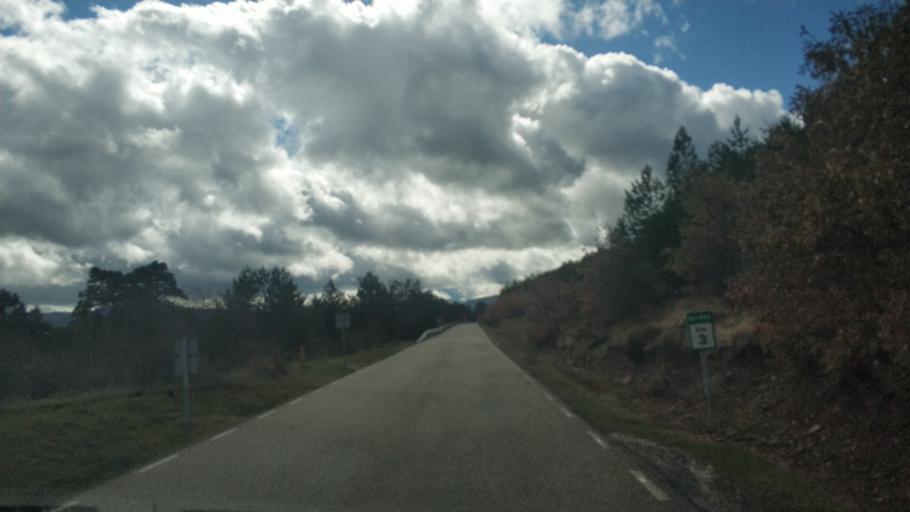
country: ES
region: Castille and Leon
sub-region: Provincia de Burgos
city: Quintanar de la Sierra
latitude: 41.9948
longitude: -3.0238
